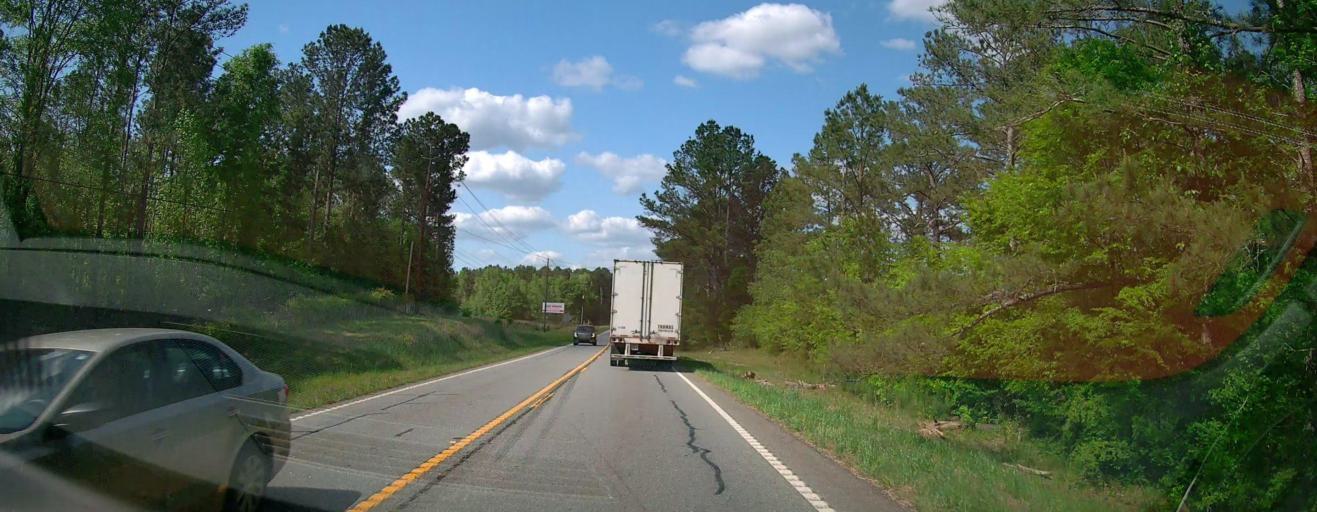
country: US
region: Georgia
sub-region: Greene County
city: Greensboro
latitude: 33.5203
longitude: -83.2227
